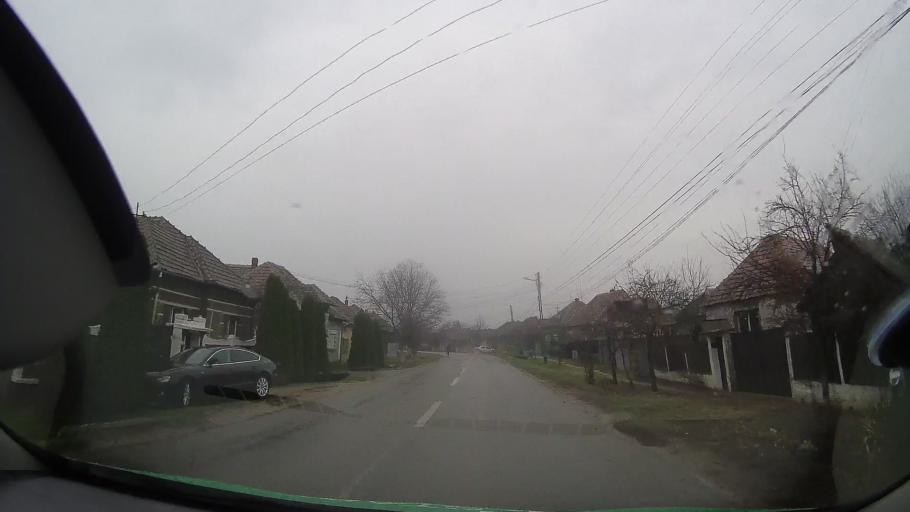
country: RO
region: Bihor
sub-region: Comuna Tulca
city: Tulca
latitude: 46.7906
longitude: 21.7721
